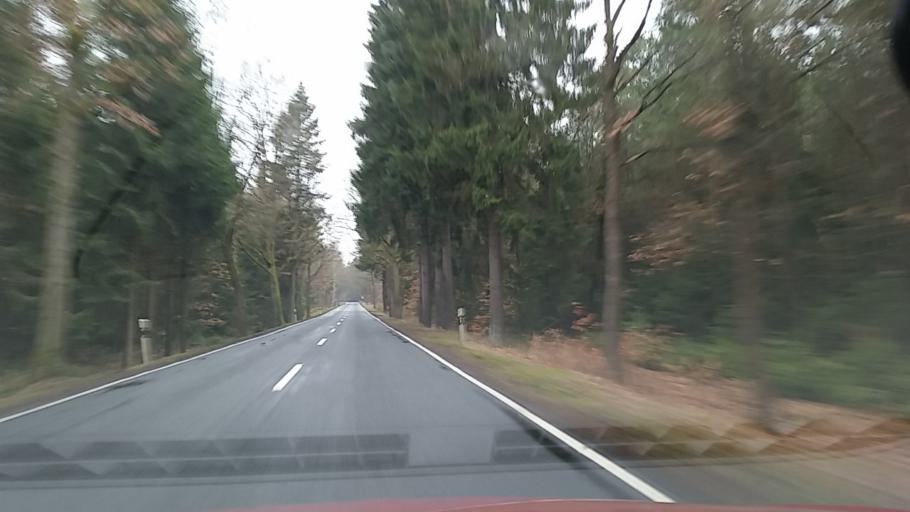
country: DE
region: Lower Saxony
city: Sprakensehl
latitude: 52.7835
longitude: 10.4143
